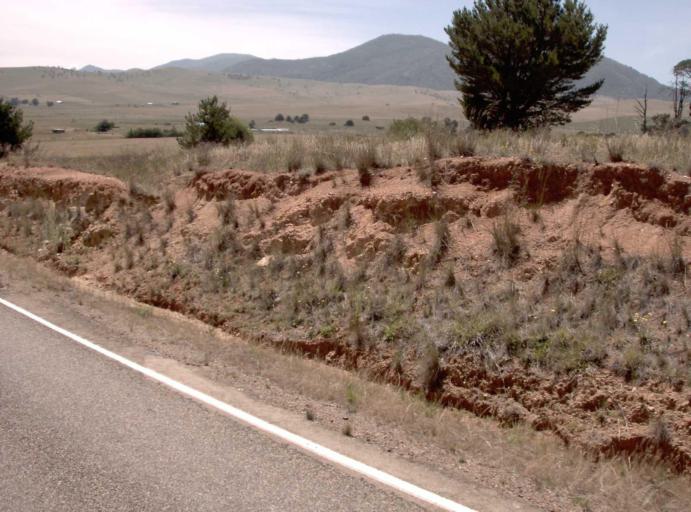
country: AU
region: Victoria
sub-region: Alpine
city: Mount Beauty
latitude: -37.0053
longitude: 147.6625
